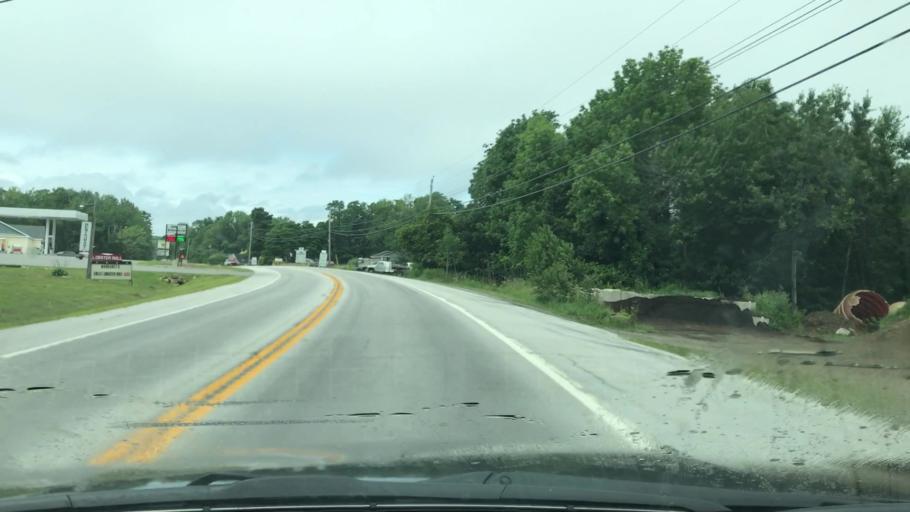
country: US
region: Maine
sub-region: Waldo County
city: Northport
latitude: 44.3354
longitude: -68.9580
